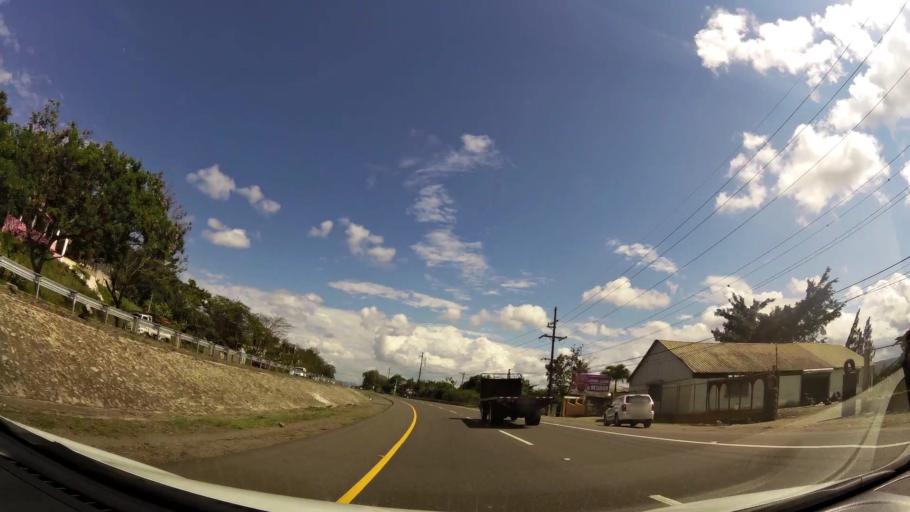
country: DO
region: La Vega
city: Concepcion de La Vega
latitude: 19.2582
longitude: -70.5693
